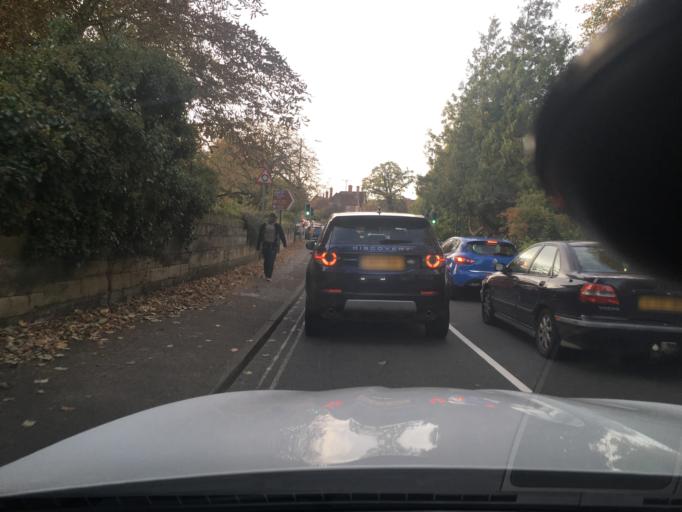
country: GB
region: England
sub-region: Warwickshire
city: Warwick
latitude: 52.2808
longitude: -1.5814
